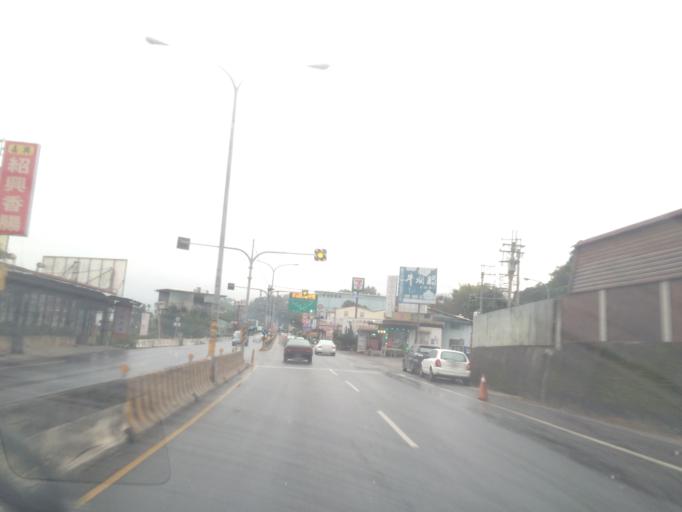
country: TW
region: Taiwan
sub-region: Nantou
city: Puli
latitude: 23.9654
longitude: 120.9363
